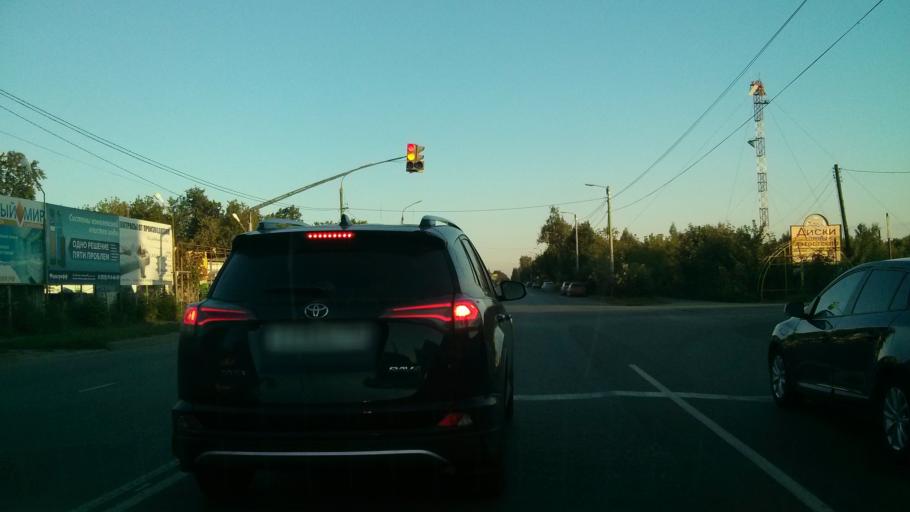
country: RU
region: Vladimir
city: Murom
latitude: 55.5621
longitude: 42.0440
